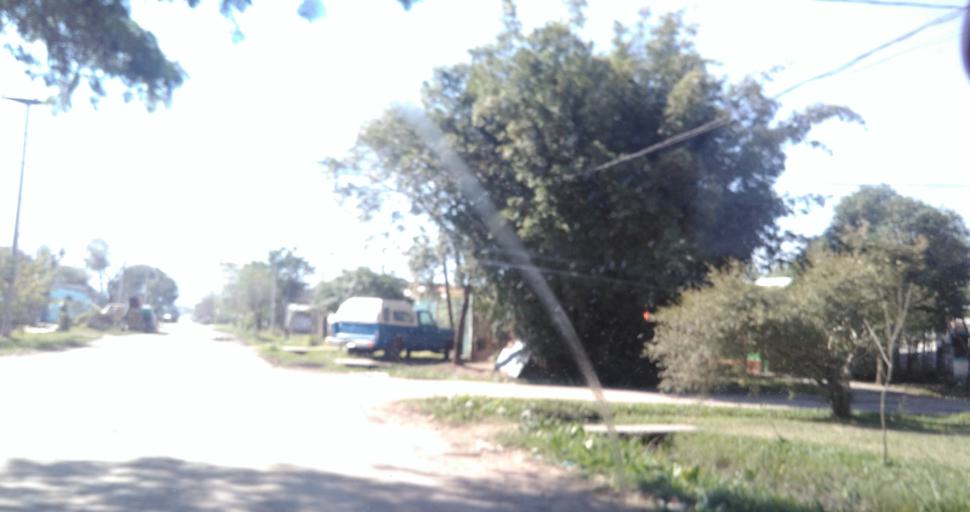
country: AR
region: Chaco
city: Fontana
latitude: -27.4514
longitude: -59.0384
